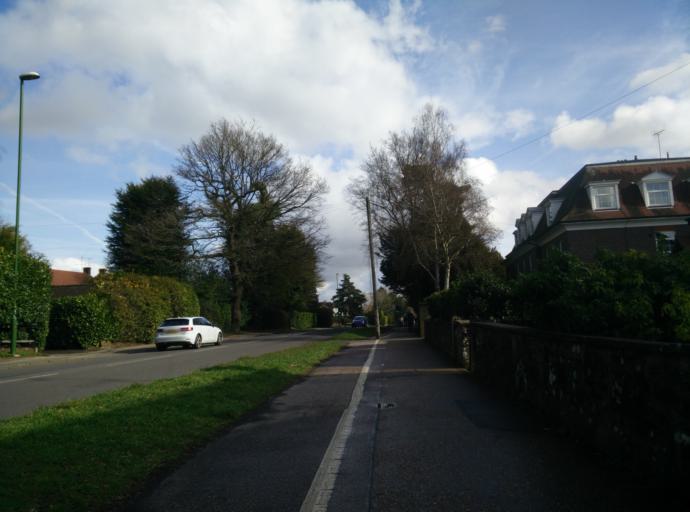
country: GB
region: England
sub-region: West Sussex
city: Horsham
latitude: 51.0656
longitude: -0.3428
